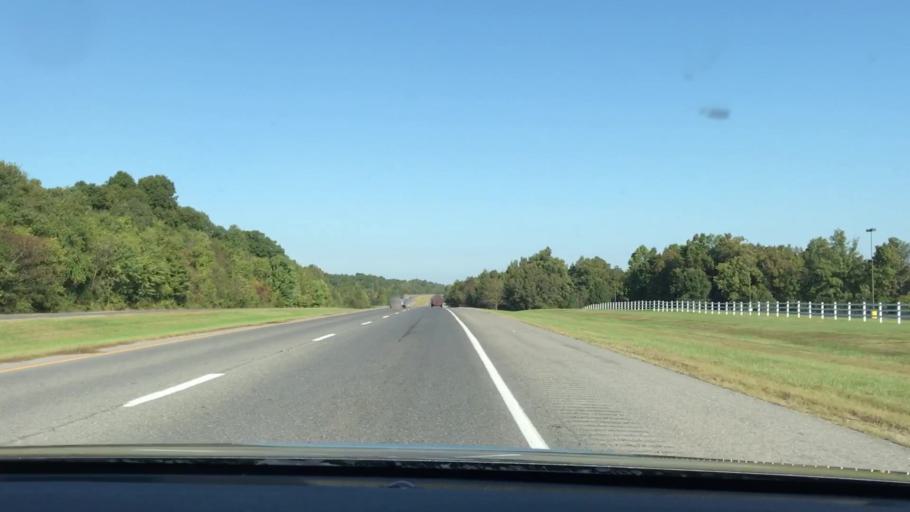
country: US
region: Kentucky
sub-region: Marshall County
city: Benton
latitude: 36.7697
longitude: -88.3143
